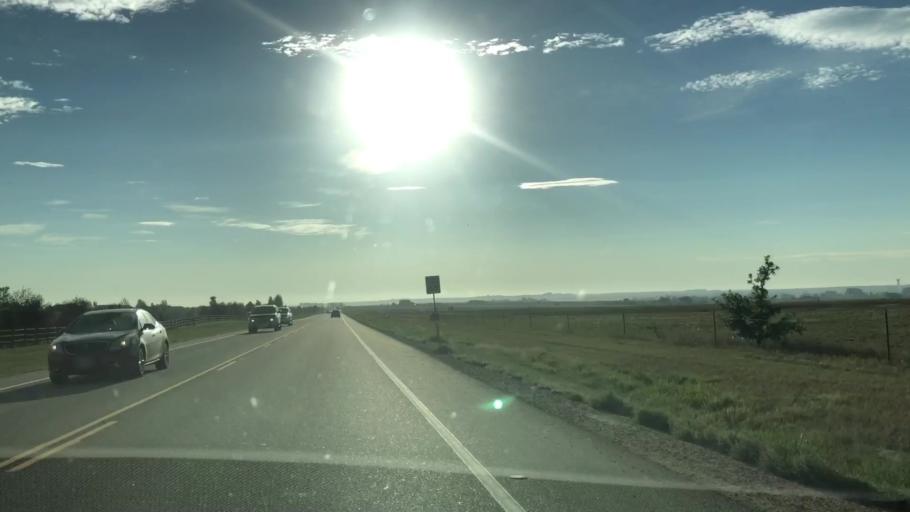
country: US
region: Colorado
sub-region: Weld County
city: Windsor
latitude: 40.4360
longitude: -104.9629
